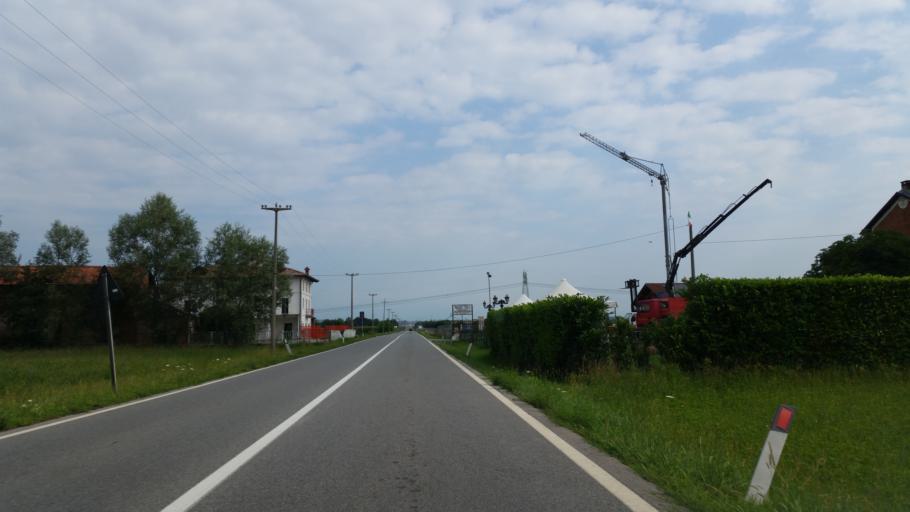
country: IT
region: Piedmont
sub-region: Provincia di Torino
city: Montanaro
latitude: 45.2550
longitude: 7.8919
